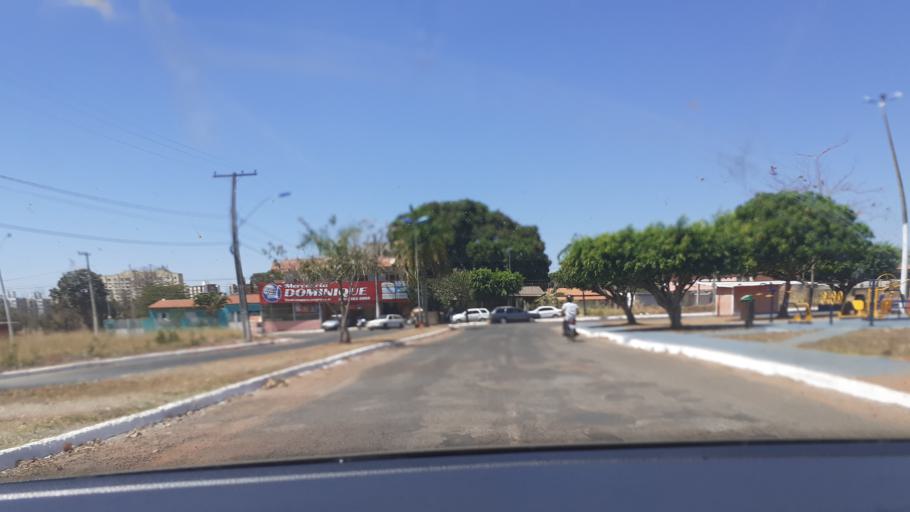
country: BR
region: Goias
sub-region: Caldas Novas
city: Caldas Novas
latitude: -17.7398
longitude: -48.6411
